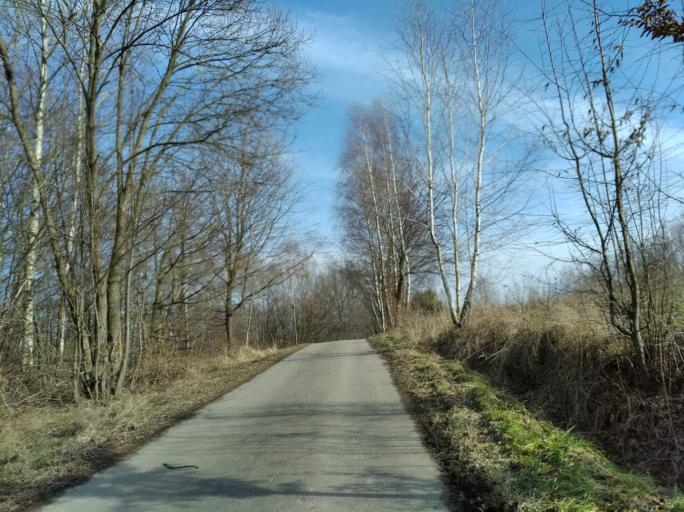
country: PL
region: Subcarpathian Voivodeship
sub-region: Powiat brzozowski
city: Gorki
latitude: 49.6442
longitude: 22.0560
